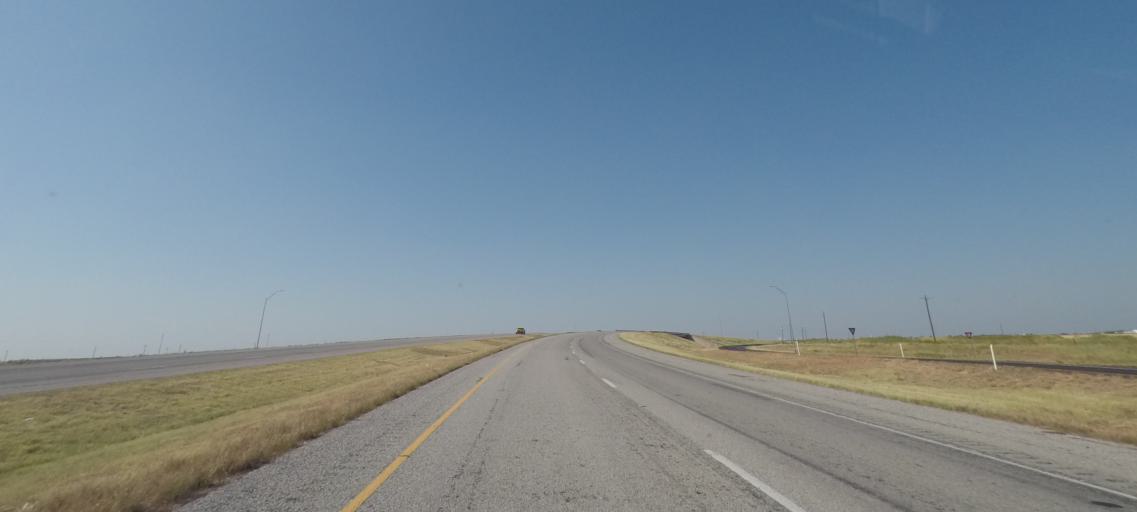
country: US
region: Texas
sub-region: Baylor County
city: Seymour
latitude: 33.6121
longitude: -99.2431
